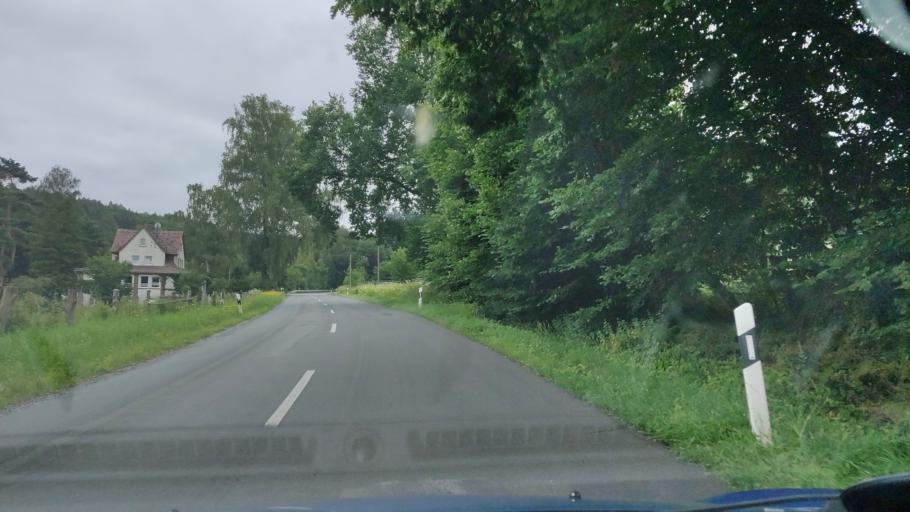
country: DE
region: Lower Saxony
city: Holzminden
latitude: 51.8077
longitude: 9.4778
